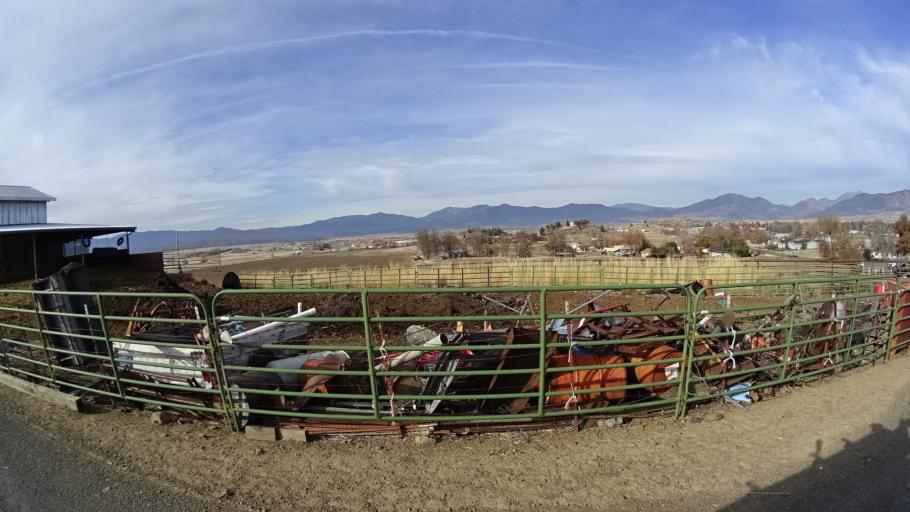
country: US
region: California
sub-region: Siskiyou County
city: Montague
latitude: 41.7190
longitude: -122.5212
